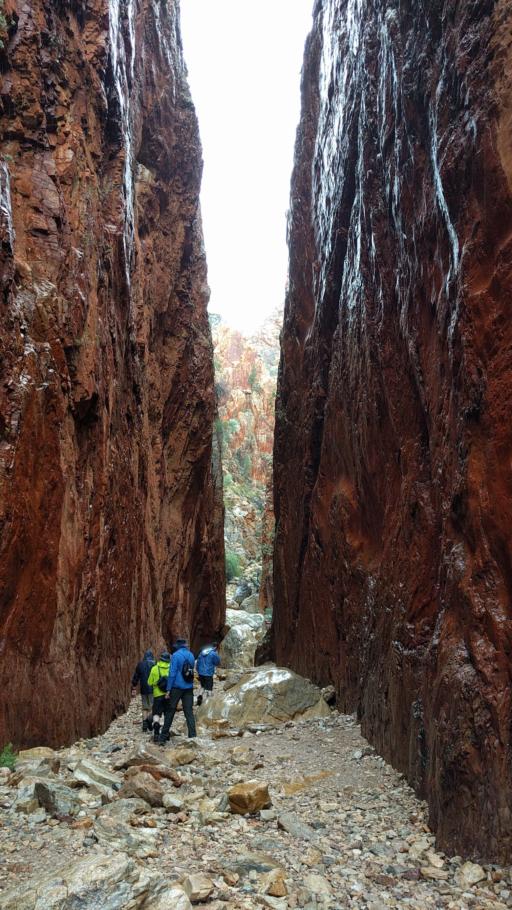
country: AU
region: Northern Territory
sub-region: Alice Springs
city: Alice Springs
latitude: -23.7150
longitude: 133.4702
